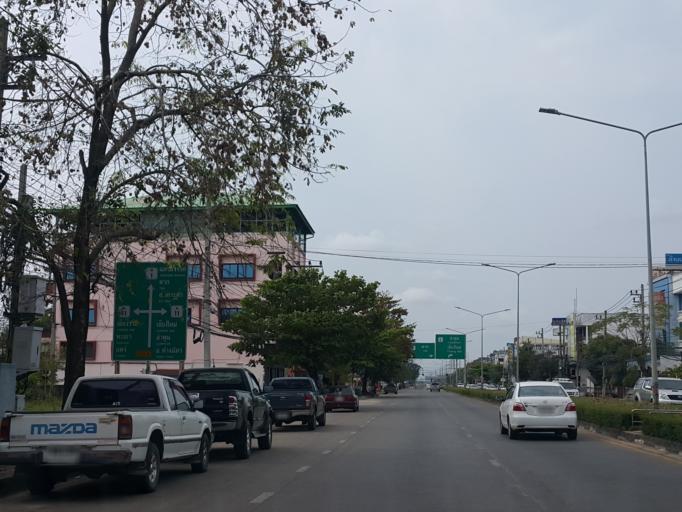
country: TH
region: Lampang
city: Lampang
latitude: 18.2705
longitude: 99.4684
